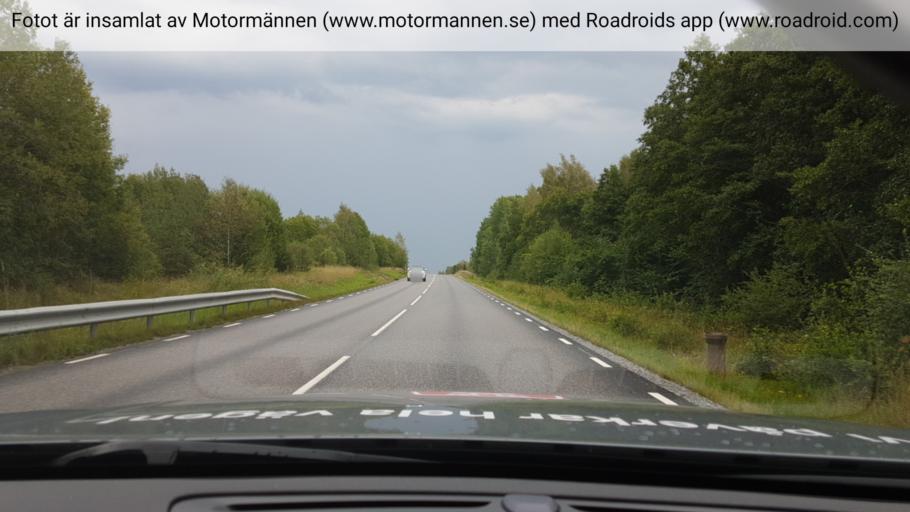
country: SE
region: Stockholm
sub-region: Upplands-Bro Kommun
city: Bro
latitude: 59.5252
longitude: 17.5867
